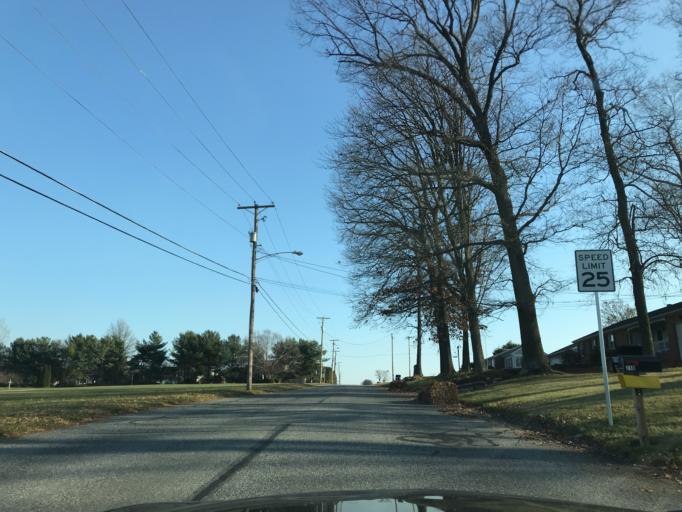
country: US
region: Pennsylvania
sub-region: York County
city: New Freedom
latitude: 39.7410
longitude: -76.6936
